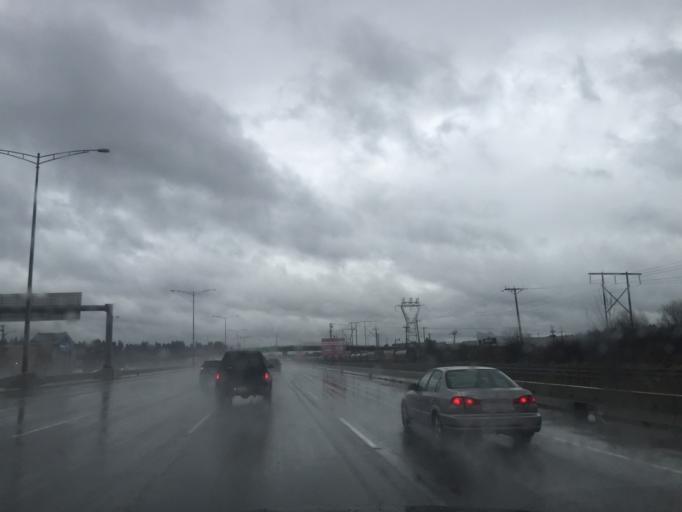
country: CA
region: British Columbia
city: New Westminster
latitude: 49.2328
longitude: -122.8676
